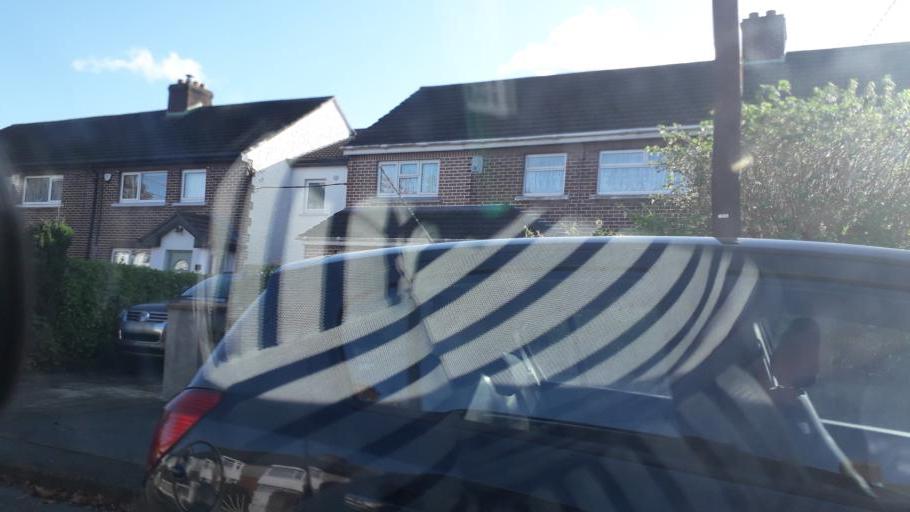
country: IE
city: Killester
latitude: 53.3778
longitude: -6.1925
